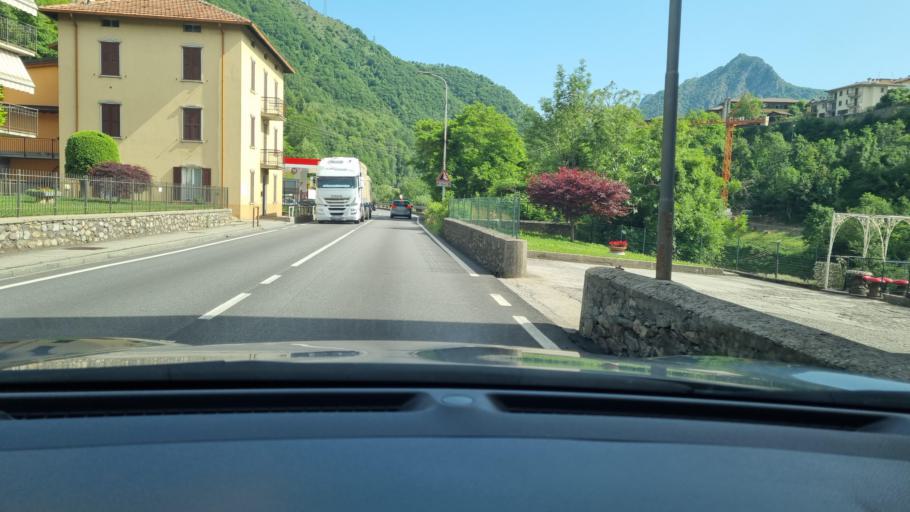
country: IT
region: Lombardy
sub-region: Provincia di Bergamo
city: Zogno
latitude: 45.7963
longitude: 9.6694
